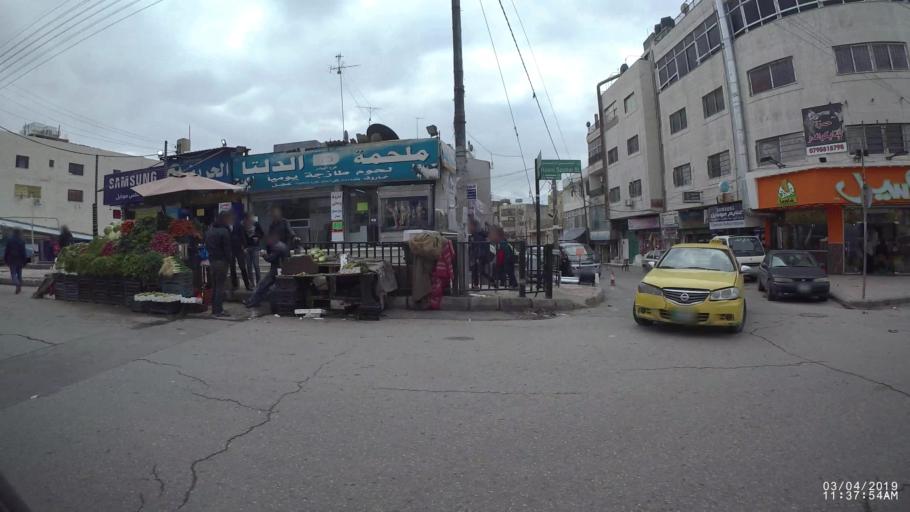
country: JO
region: Amman
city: Wadi as Sir
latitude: 31.9543
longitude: 35.8346
